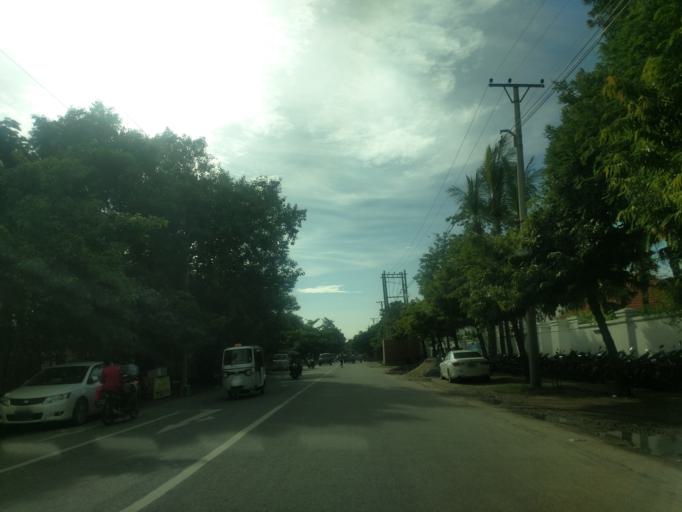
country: MM
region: Mandalay
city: Mandalay
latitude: 21.9804
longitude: 96.1062
